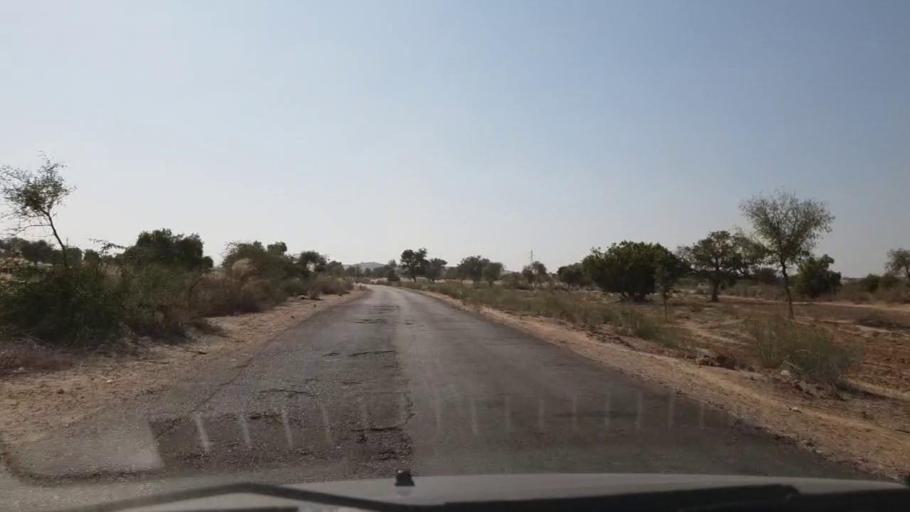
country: PK
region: Sindh
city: Mithi
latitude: 24.6613
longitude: 69.7577
